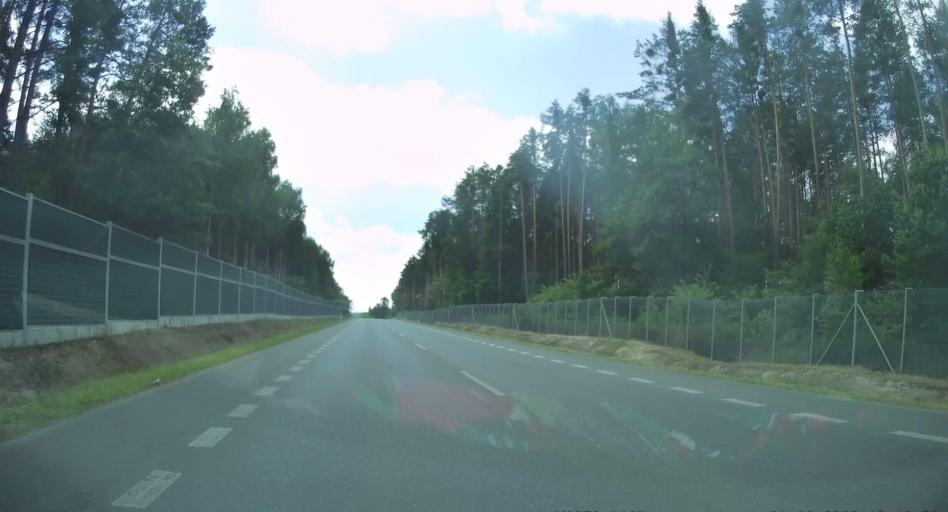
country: PL
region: Subcarpathian Voivodeship
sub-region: Powiat mielecki
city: Mielec
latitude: 50.2664
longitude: 21.4942
